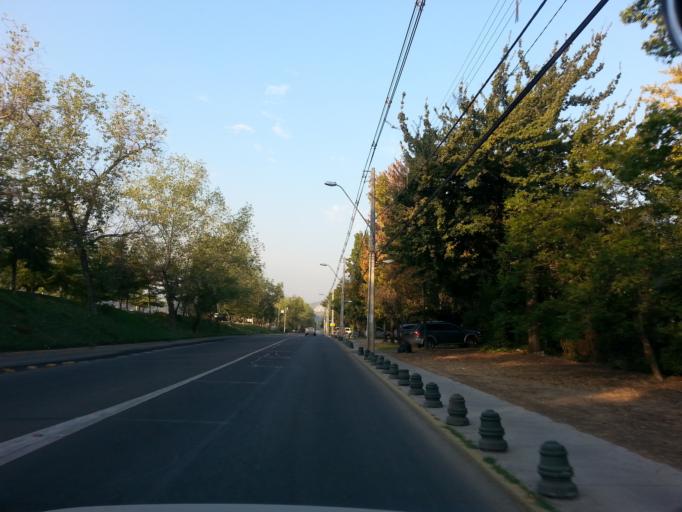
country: CL
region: Santiago Metropolitan
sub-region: Provincia de Santiago
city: Villa Presidente Frei, Nunoa, Santiago, Chile
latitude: -33.3814
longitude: -70.5773
